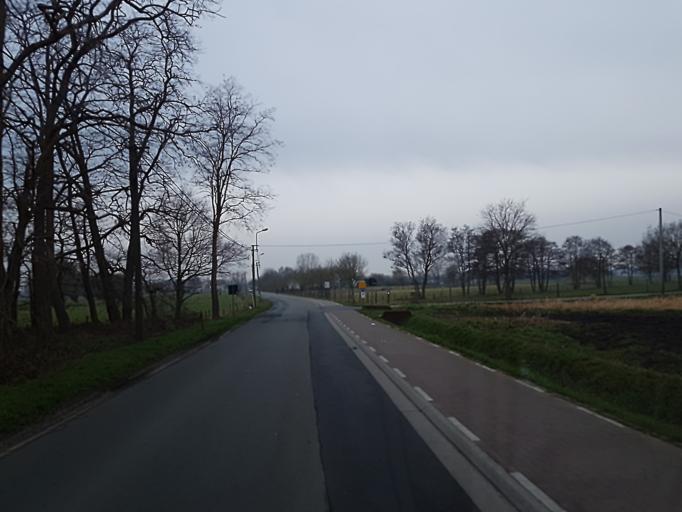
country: BE
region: Flanders
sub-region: Provincie Oost-Vlaanderen
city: Waarschoot
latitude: 51.1730
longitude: 3.6193
